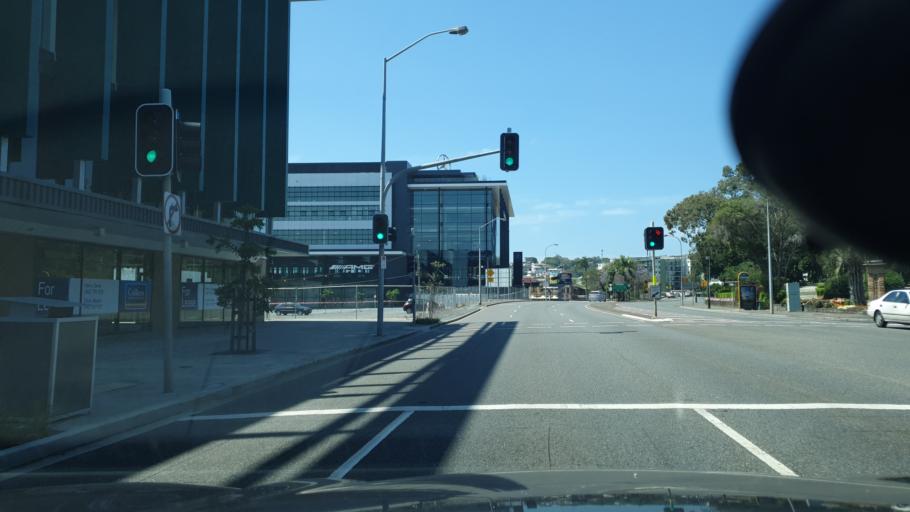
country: AU
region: Queensland
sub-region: Brisbane
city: Windsor
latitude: -27.4432
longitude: 153.0440
